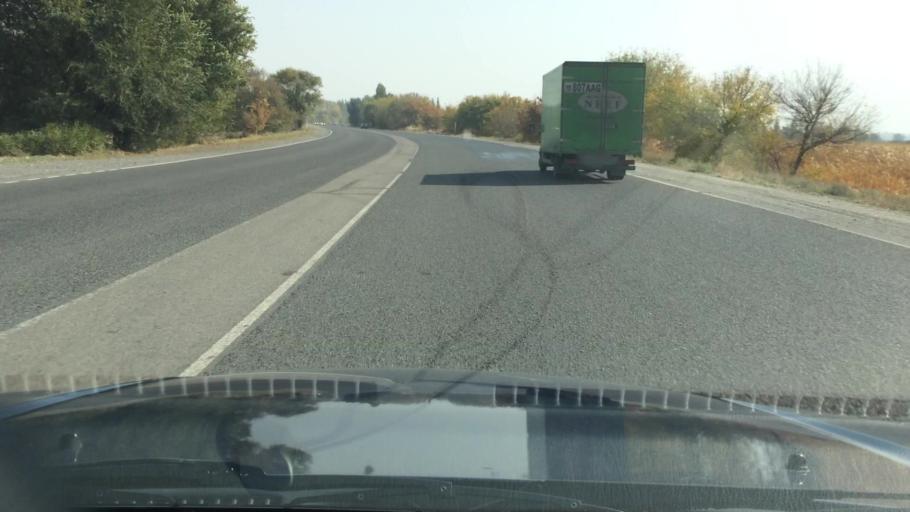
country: KG
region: Chuy
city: Ivanovka
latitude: 42.9398
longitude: 74.9722
